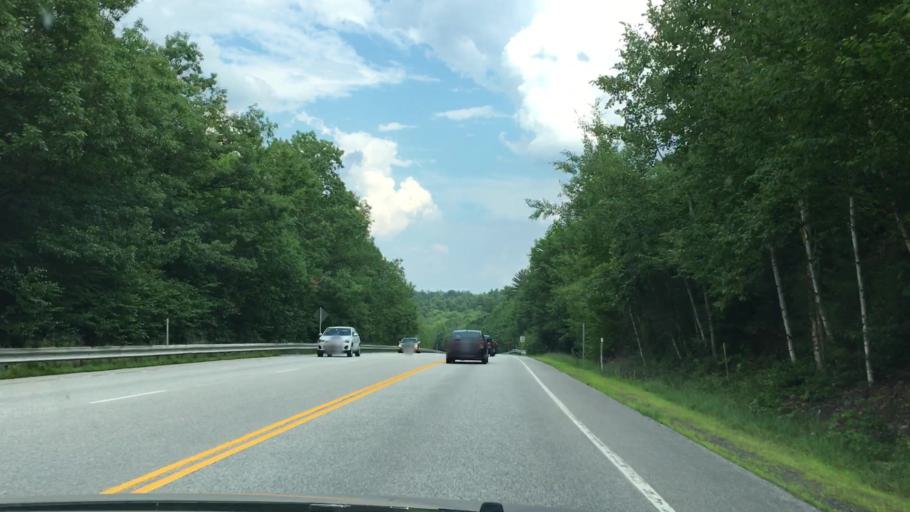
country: US
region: New Hampshire
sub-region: Belknap County
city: Gilford
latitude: 43.5738
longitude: -71.3611
